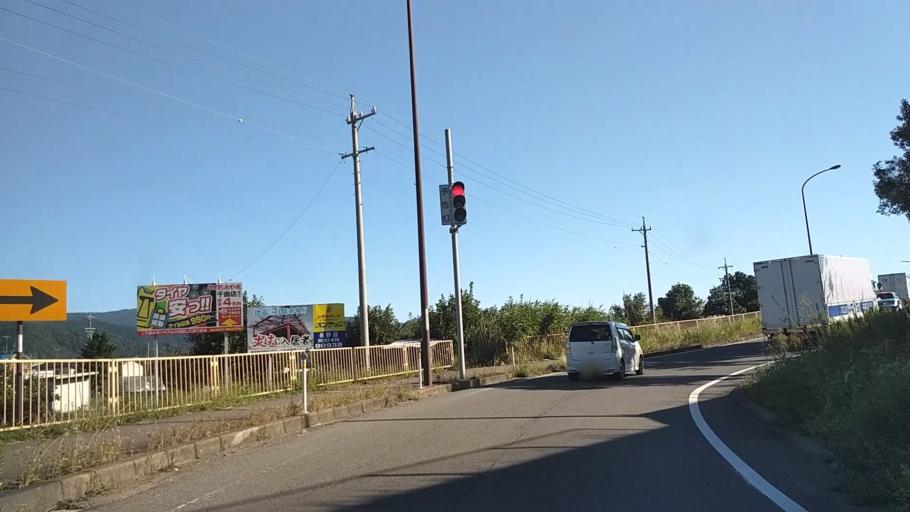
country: JP
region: Nagano
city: Nagano-shi
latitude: 36.5618
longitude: 138.1389
